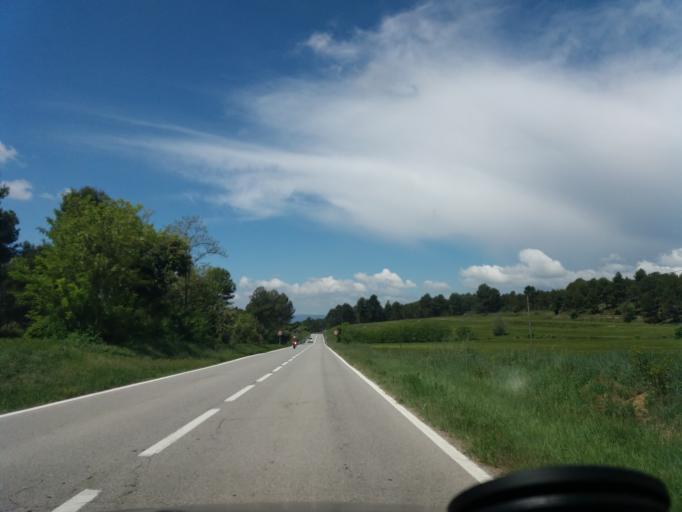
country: ES
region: Catalonia
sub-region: Provincia de Barcelona
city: Artes
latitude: 41.7781
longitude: 1.9736
